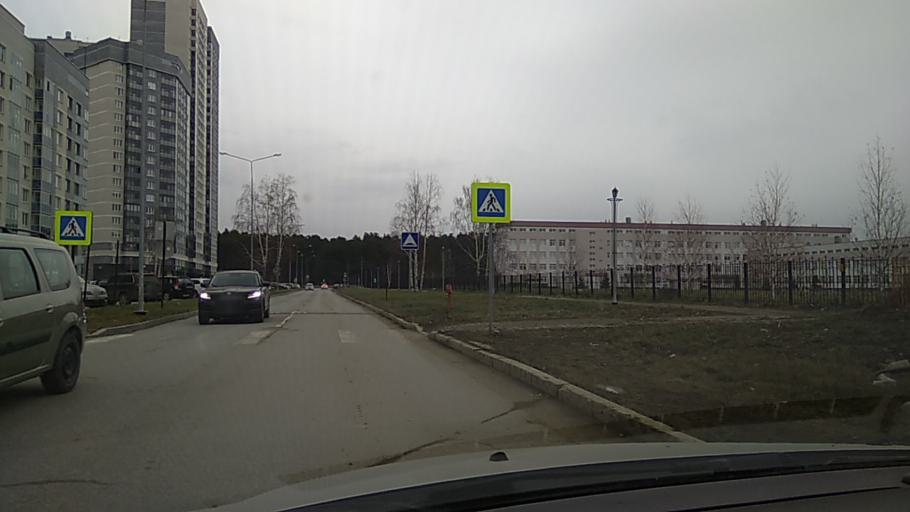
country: RU
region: Sverdlovsk
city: Sovkhoznyy
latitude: 56.7807
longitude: 60.5517
